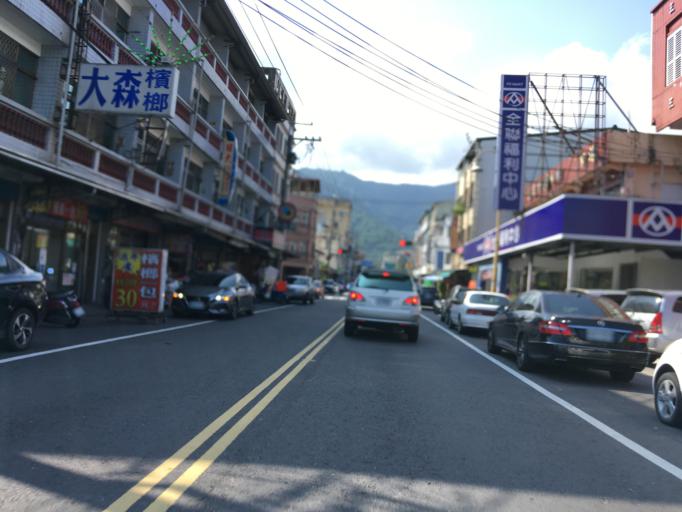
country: TW
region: Taiwan
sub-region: Yilan
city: Yilan
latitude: 24.6681
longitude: 121.6525
